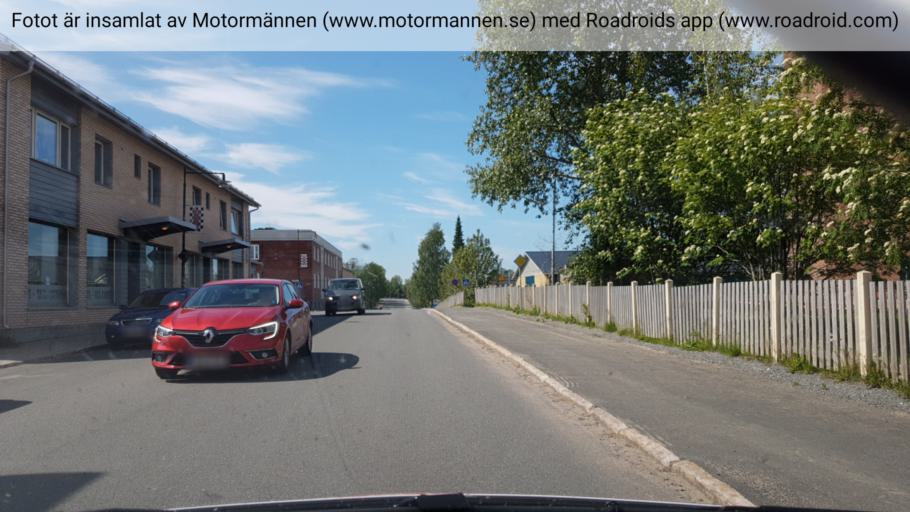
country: SE
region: Norrbotten
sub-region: Haparanda Kommun
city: Haparanda
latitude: 65.8353
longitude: 24.1335
